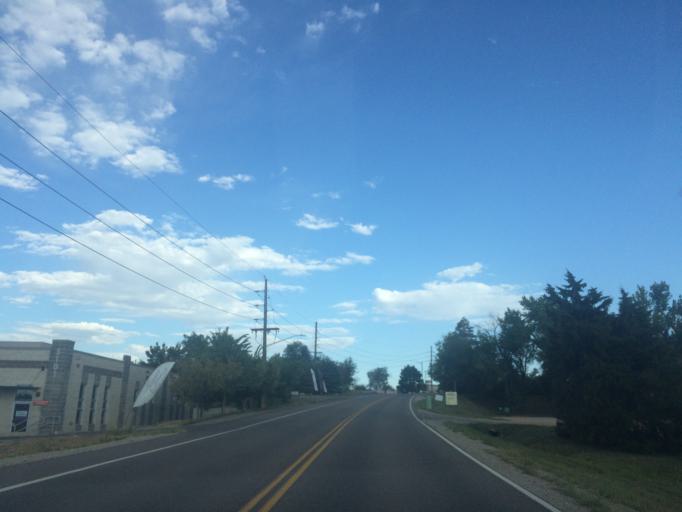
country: US
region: Colorado
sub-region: Broomfield County
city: Broomfield
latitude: 39.9224
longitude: -105.1044
